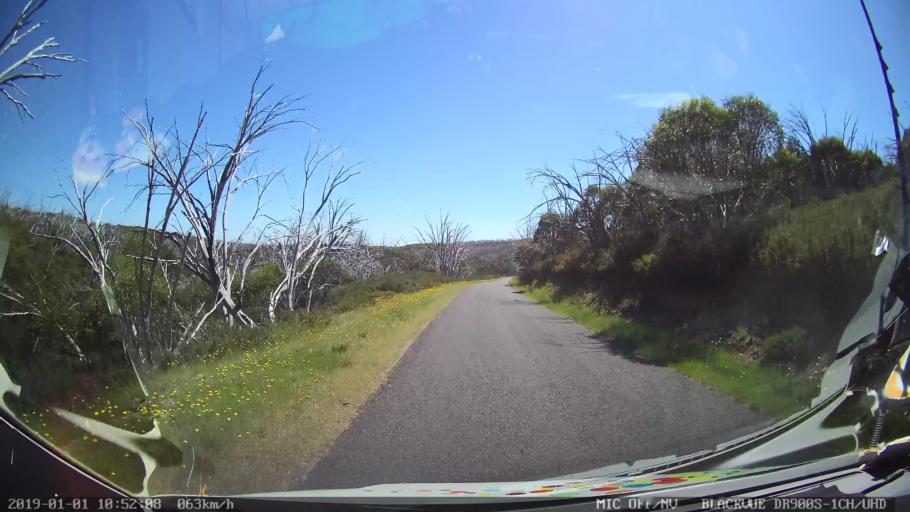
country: AU
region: New South Wales
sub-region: Snowy River
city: Jindabyne
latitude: -36.0175
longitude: 148.3775
